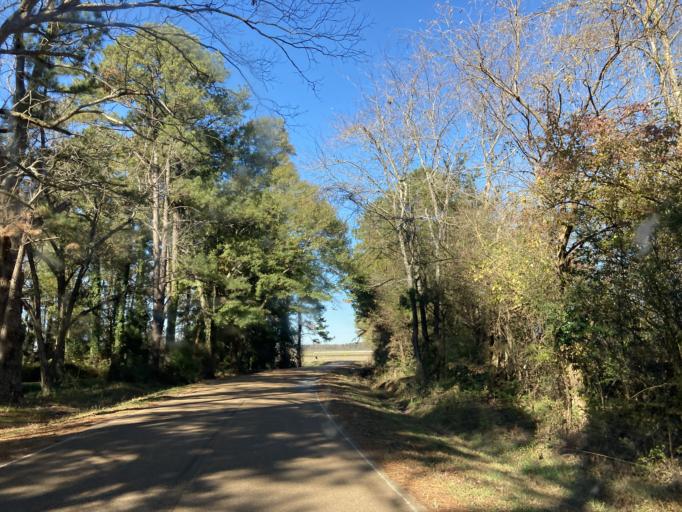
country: US
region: Mississippi
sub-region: Hinds County
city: Lynchburg
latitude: 32.6200
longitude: -90.5743
